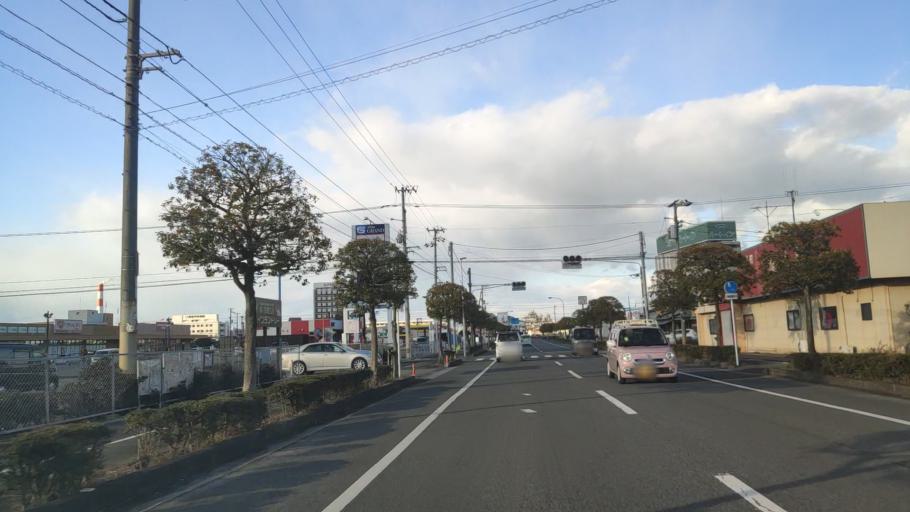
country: JP
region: Ehime
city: Saijo
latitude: 33.9256
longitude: 133.1837
